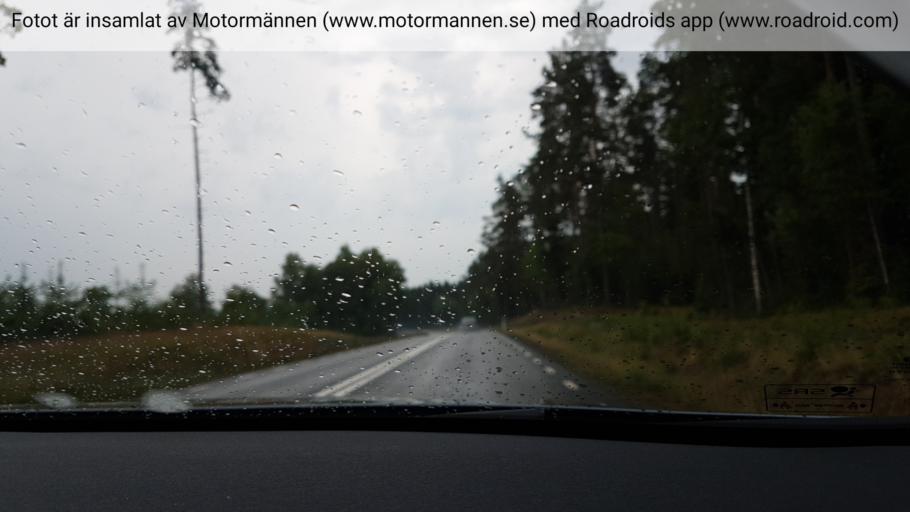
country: SE
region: Joenkoeping
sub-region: Vaggeryds Kommun
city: Vaggeryd
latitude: 57.4906
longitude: 14.2967
